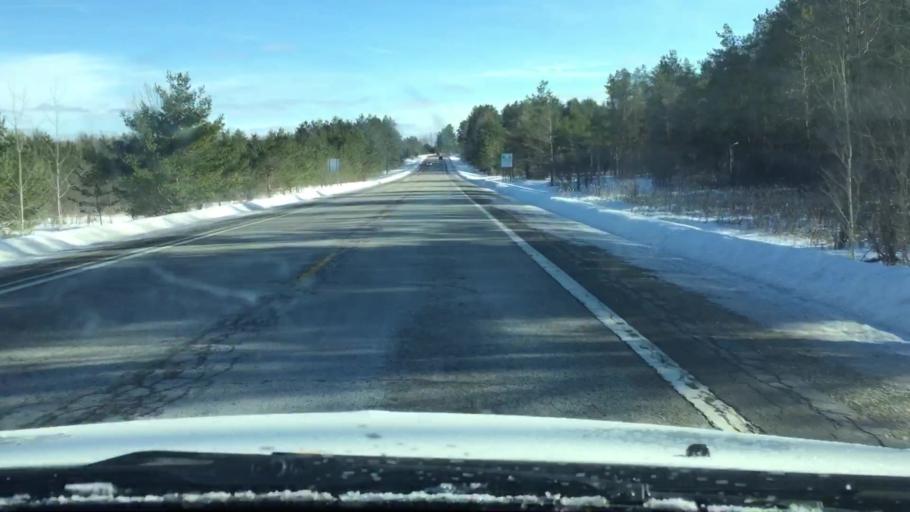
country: US
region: Michigan
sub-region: Charlevoix County
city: East Jordan
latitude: 45.0966
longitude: -85.1051
